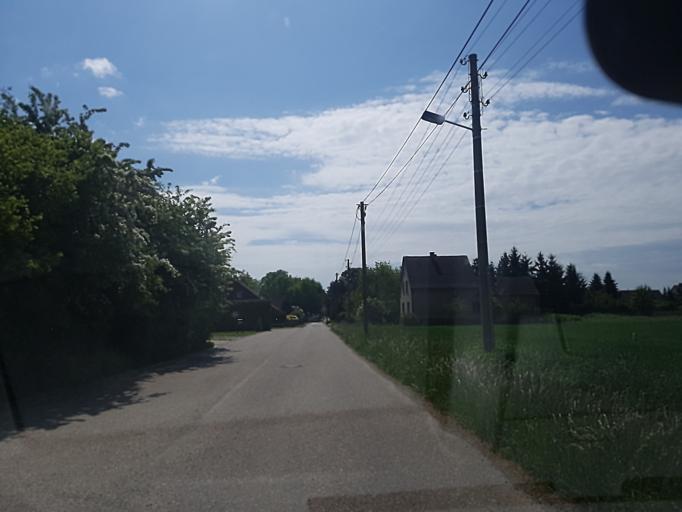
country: DE
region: Brandenburg
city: Doberlug-Kirchhain
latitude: 51.6358
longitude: 13.5523
